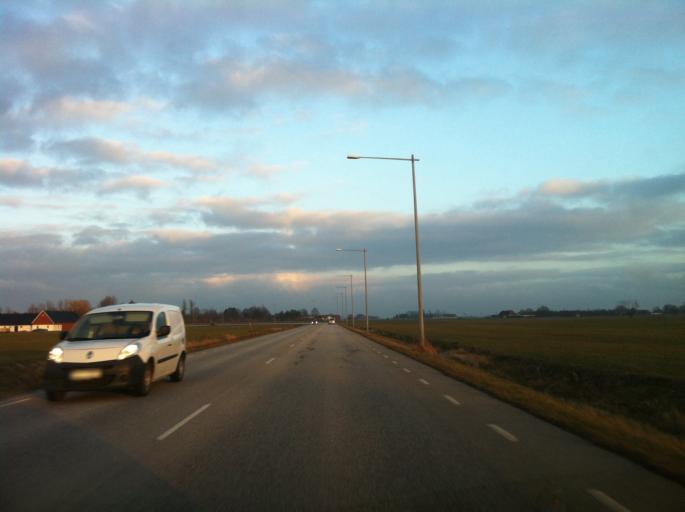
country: SE
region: Skane
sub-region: Kavlinge Kommun
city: Loddekopinge
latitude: 55.7744
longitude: 13.0024
